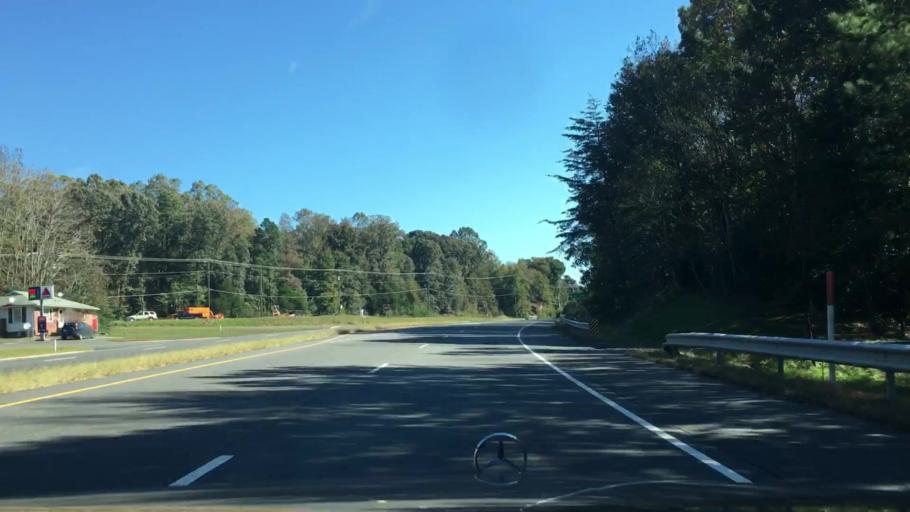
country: US
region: Virginia
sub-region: King George County
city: King George
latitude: 38.2801
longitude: -77.2225
